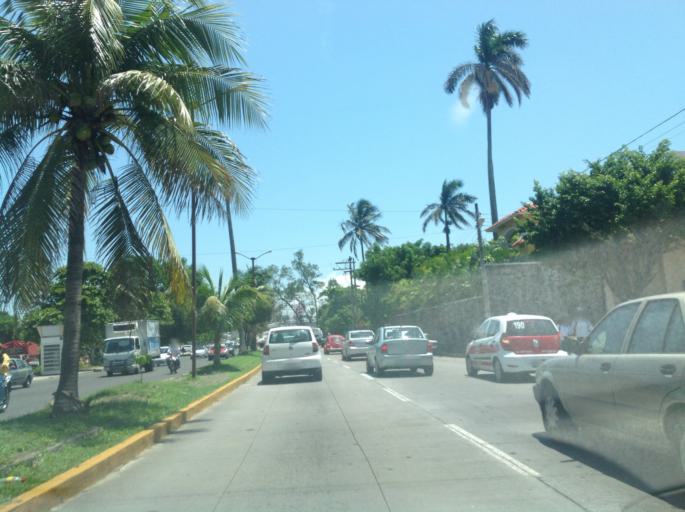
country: MX
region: Veracruz
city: Veracruz
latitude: 19.1518
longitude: -96.1300
